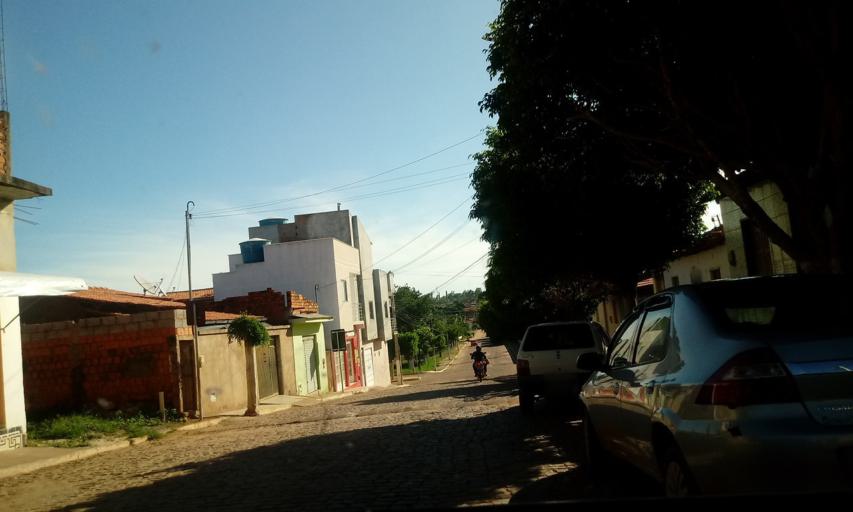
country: BR
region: Bahia
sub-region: Riacho De Santana
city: Riacho de Santana
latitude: -13.7734
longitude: -42.7169
